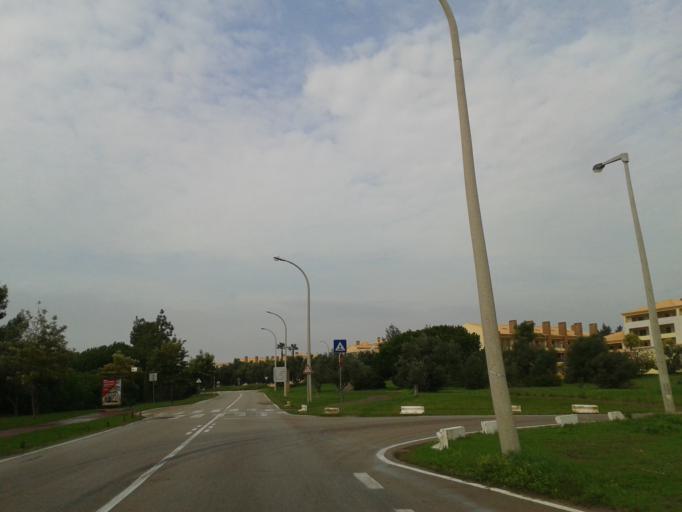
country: PT
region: Faro
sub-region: Loule
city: Vilamoura
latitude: 37.1045
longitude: -8.1285
